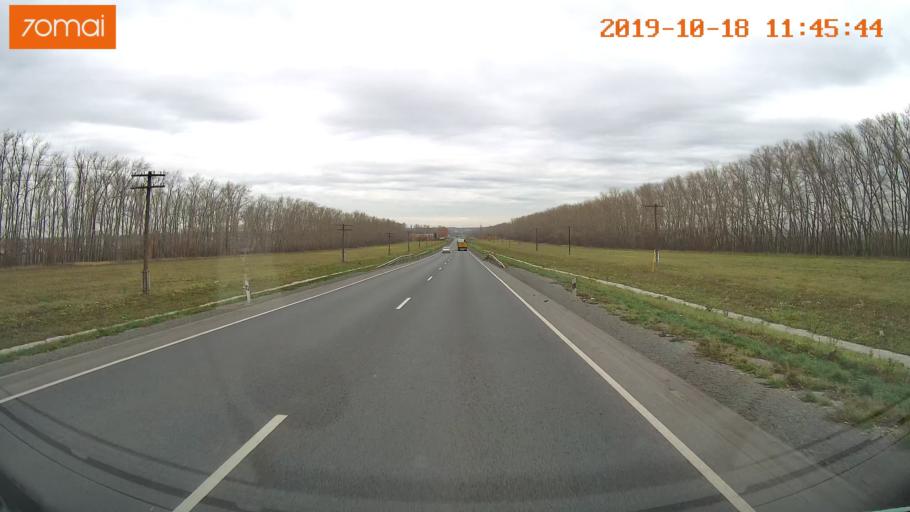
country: RU
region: Rjazan
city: Mikhaylov
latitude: 54.2131
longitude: 38.9739
